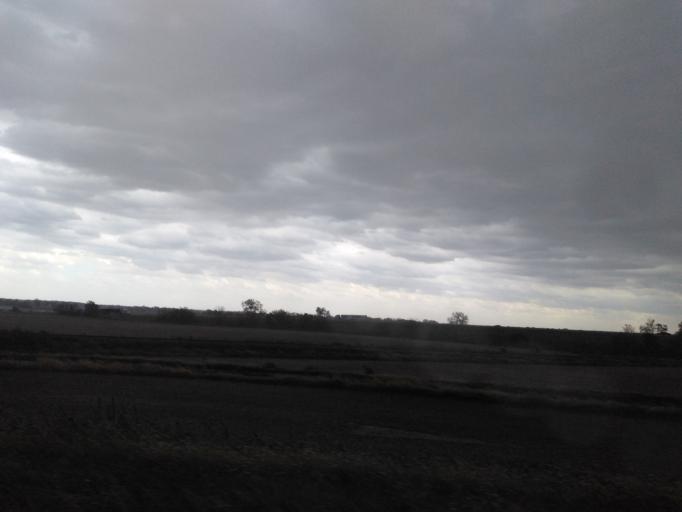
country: US
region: Illinois
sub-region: Bond County
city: Greenville
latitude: 38.8566
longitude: -89.4456
